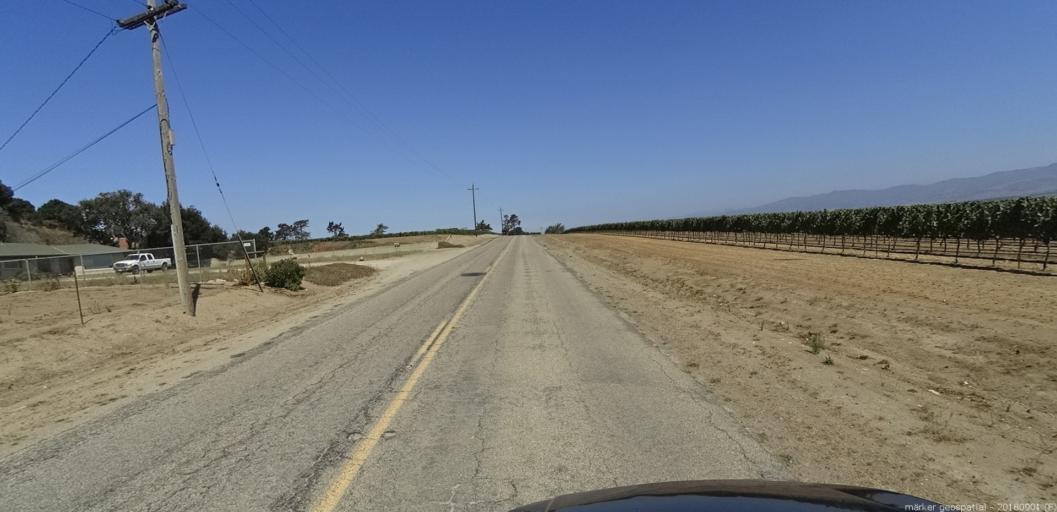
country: US
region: California
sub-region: Monterey County
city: Chualar
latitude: 36.5175
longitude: -121.5197
